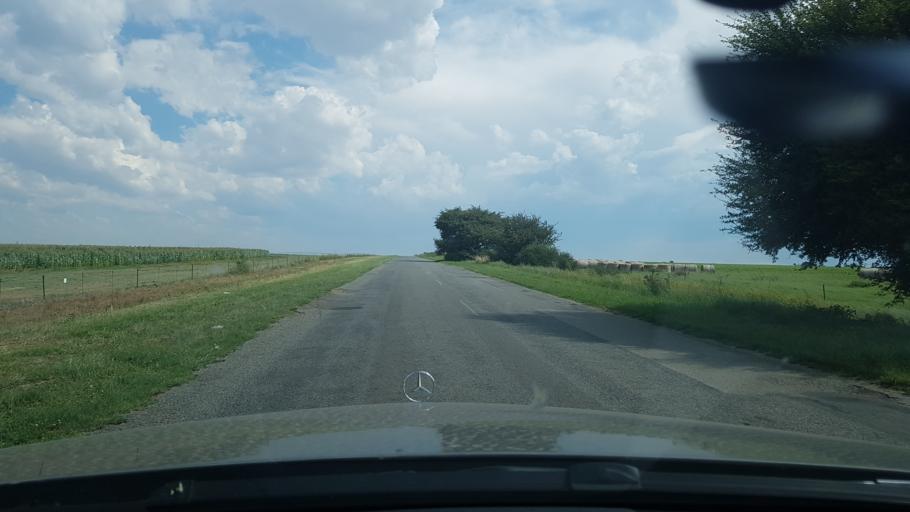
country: ZA
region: North-West
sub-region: Dr Ruth Segomotsi Mompati District Municipality
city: Bloemhof
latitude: -27.6647
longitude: 25.5925
